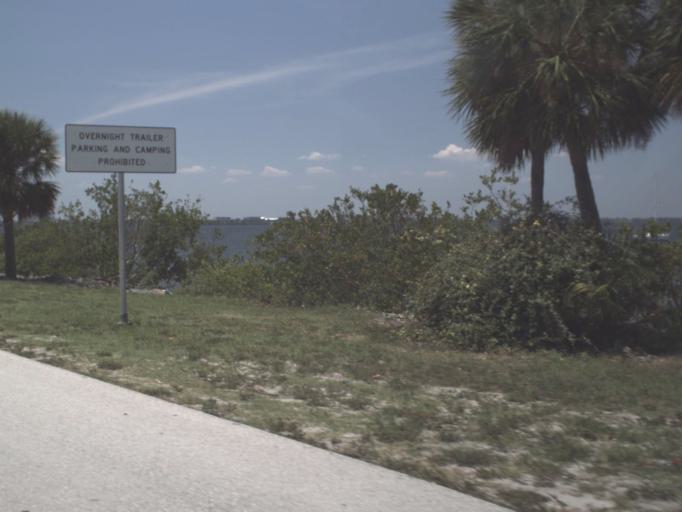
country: US
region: Florida
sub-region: Brevard County
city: Indialantic
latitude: 28.0879
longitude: -80.5806
